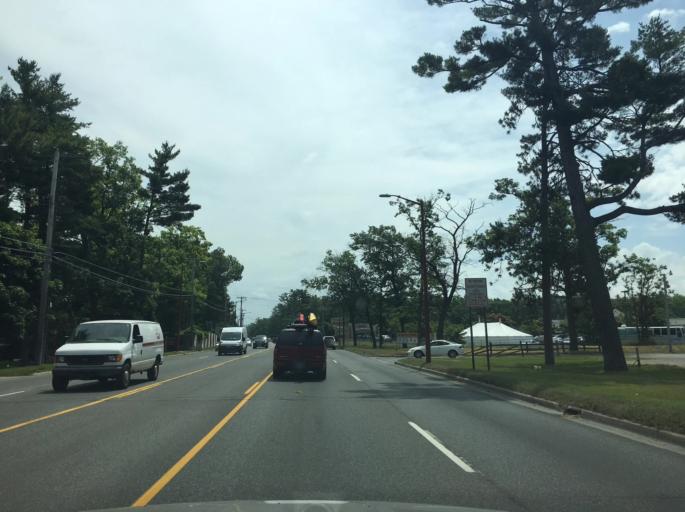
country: US
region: Michigan
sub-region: Grand Traverse County
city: Traverse City
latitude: 44.7558
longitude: -85.5743
